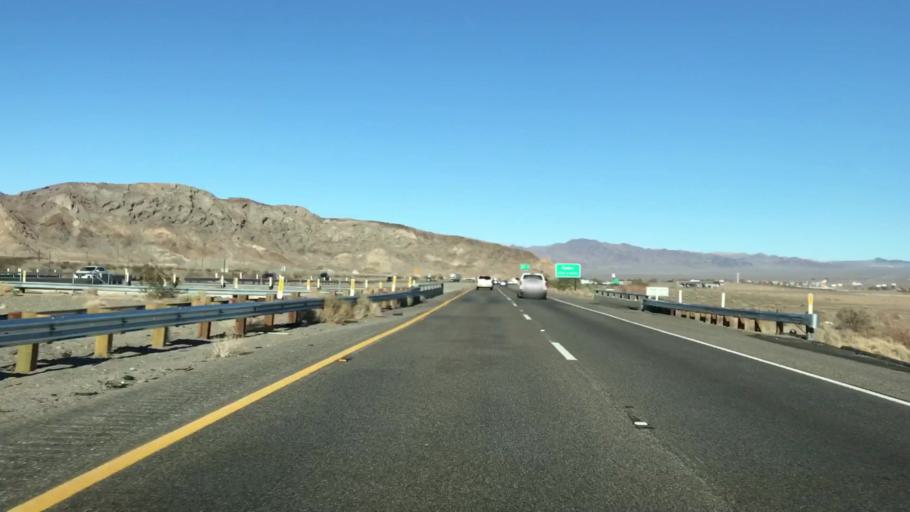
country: US
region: California
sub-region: San Bernardino County
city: Fort Irwin
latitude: 35.2474
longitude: -116.0915
